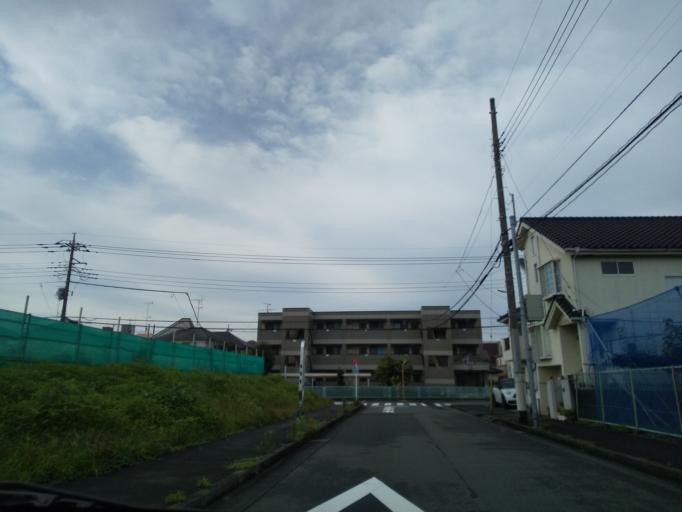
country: JP
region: Tokyo
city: Hino
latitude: 35.6718
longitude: 139.4113
